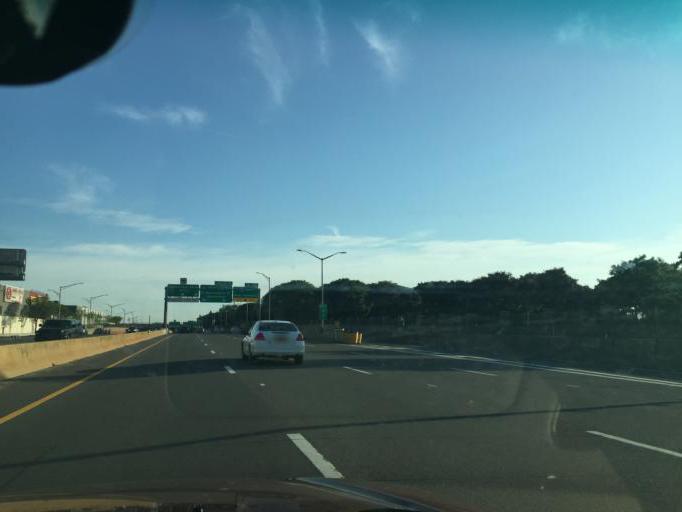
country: US
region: New York
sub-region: Bronx
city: The Bronx
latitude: 40.8211
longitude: -73.8361
